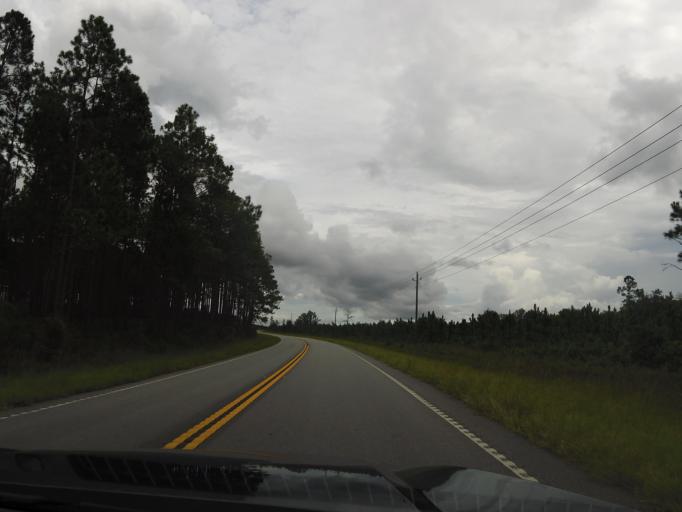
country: US
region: Florida
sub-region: Baker County
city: Macclenny
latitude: 30.5183
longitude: -82.1379
